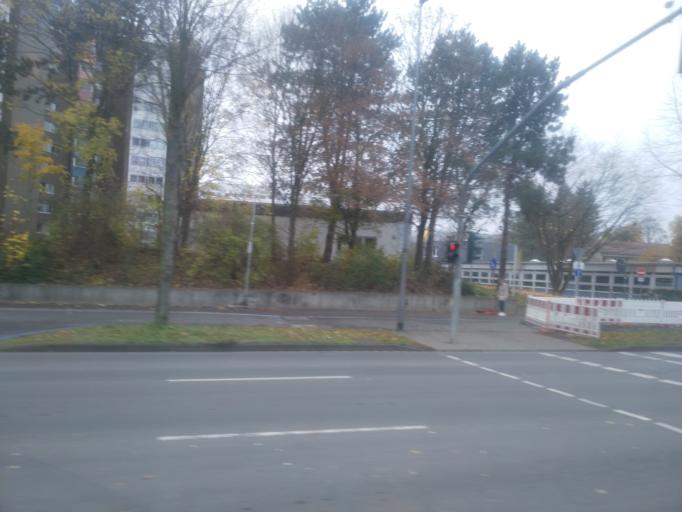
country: DE
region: Lower Saxony
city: Goettingen
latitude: 51.5492
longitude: 9.9387
